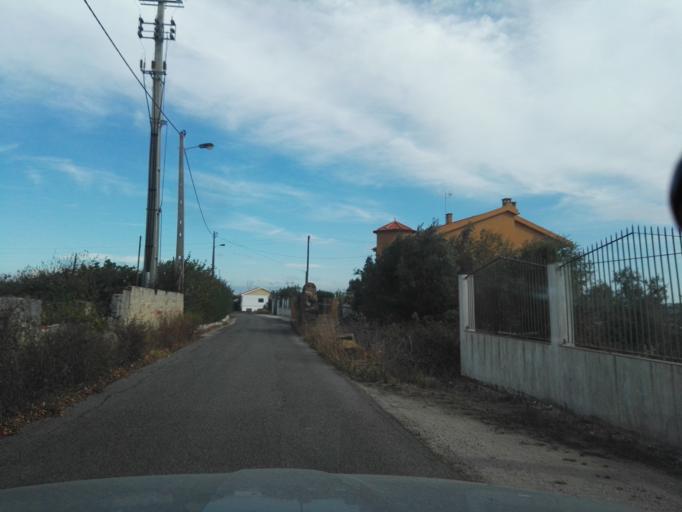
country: PT
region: Lisbon
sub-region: Vila Franca de Xira
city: Sao Joao dos Montes
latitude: 38.9690
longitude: -9.0164
